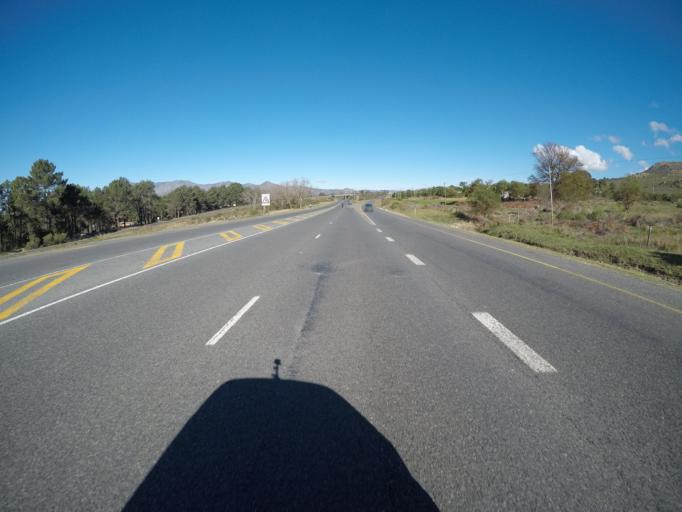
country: ZA
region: Western Cape
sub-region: Overberg District Municipality
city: Grabouw
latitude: -34.2266
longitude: 19.1877
